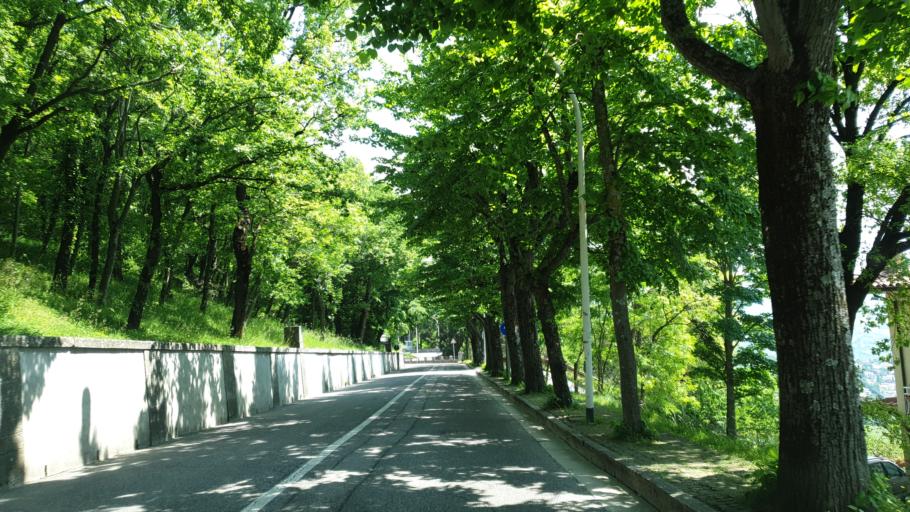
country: SM
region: San Marino
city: San Marino
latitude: 43.9310
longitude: 12.4504
